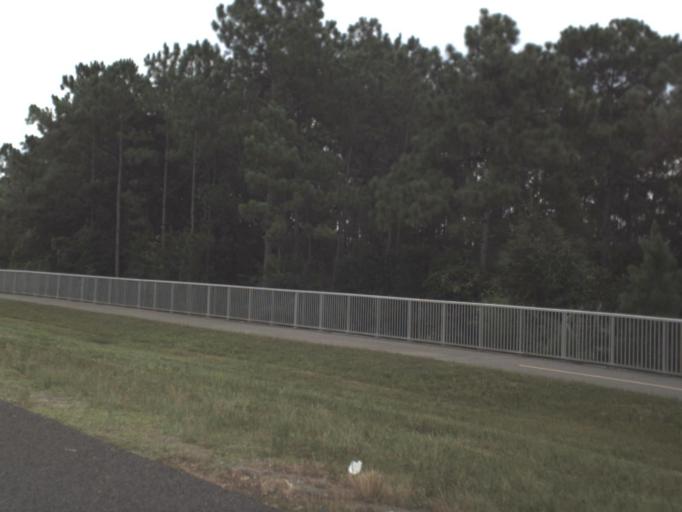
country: US
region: Florida
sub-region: Hillsborough County
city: Pebble Creek
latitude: 28.1859
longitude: -82.3501
